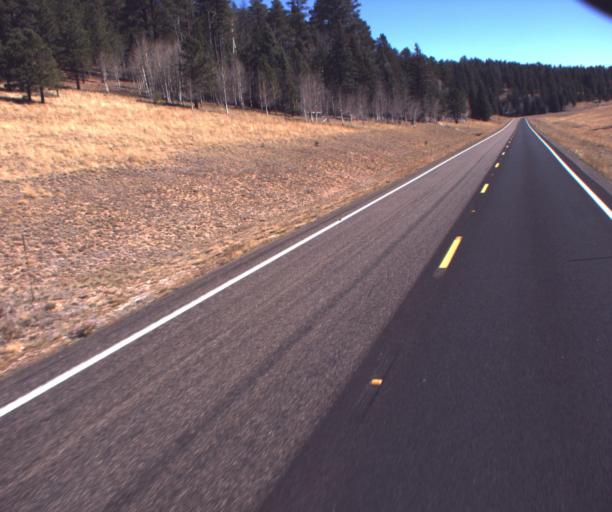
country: US
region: Arizona
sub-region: Coconino County
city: Grand Canyon
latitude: 36.5425
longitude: -112.1649
